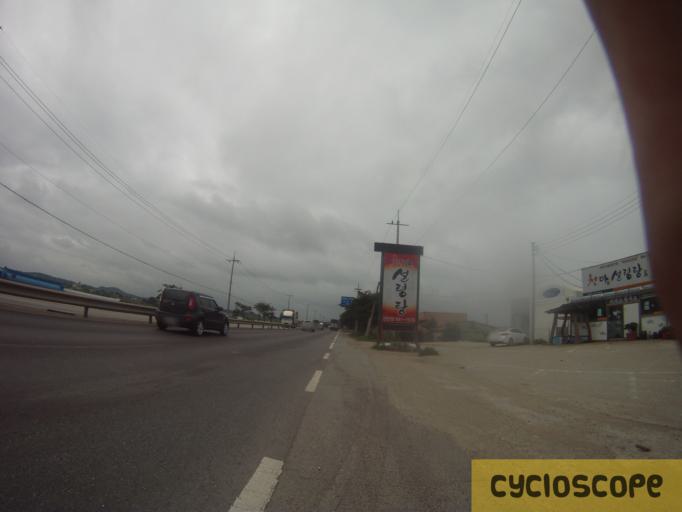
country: KR
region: Gyeonggi-do
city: Hwaseong-si
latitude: 37.0071
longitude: 126.8209
